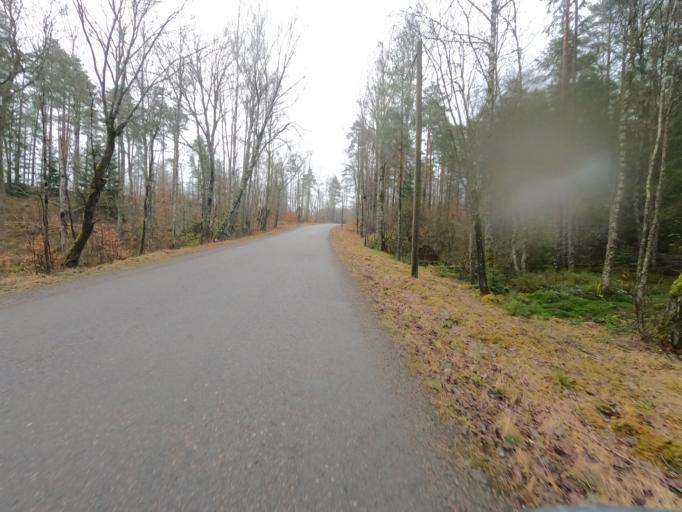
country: SE
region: Halland
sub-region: Hylte Kommun
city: Hyltebruk
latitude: 56.8421
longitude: 13.4692
